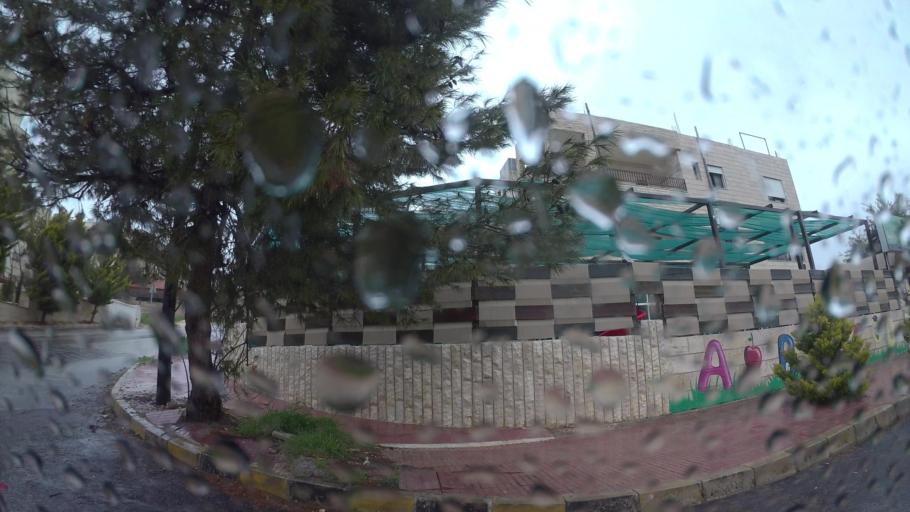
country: JO
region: Amman
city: Al Jubayhah
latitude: 32.0468
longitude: 35.8907
